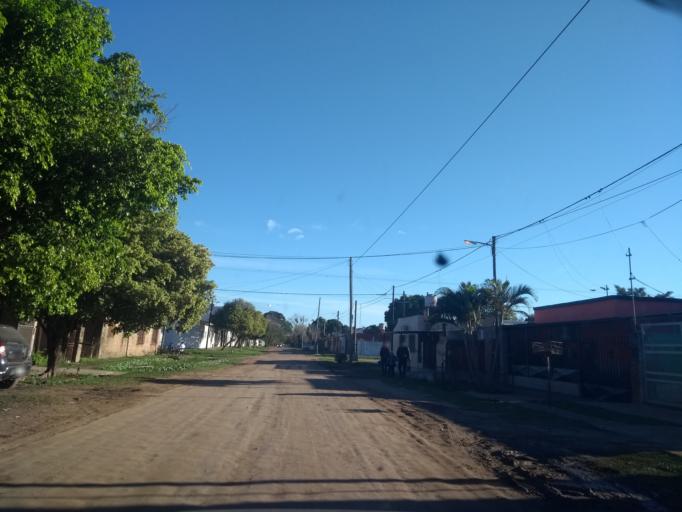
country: AR
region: Chaco
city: Barranqueras
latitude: -27.4791
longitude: -58.9338
